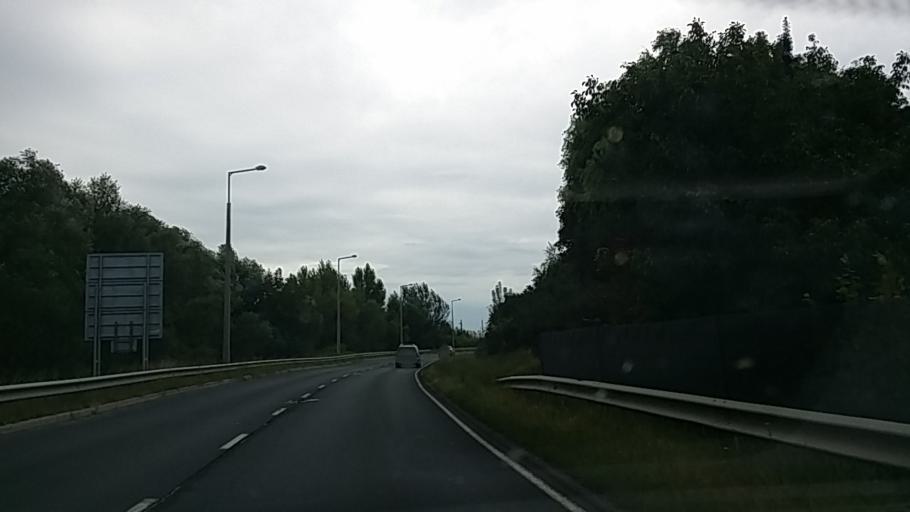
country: HU
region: Gyor-Moson-Sopron
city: Fertoszentmiklos
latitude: 47.5885
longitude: 16.8735
